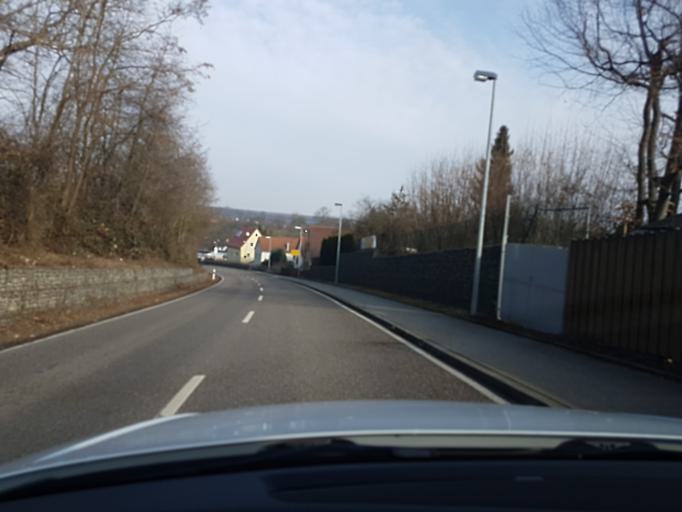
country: DE
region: Baden-Wuerttemberg
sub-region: Regierungsbezirk Stuttgart
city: Nordheim
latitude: 49.1020
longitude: 9.1364
